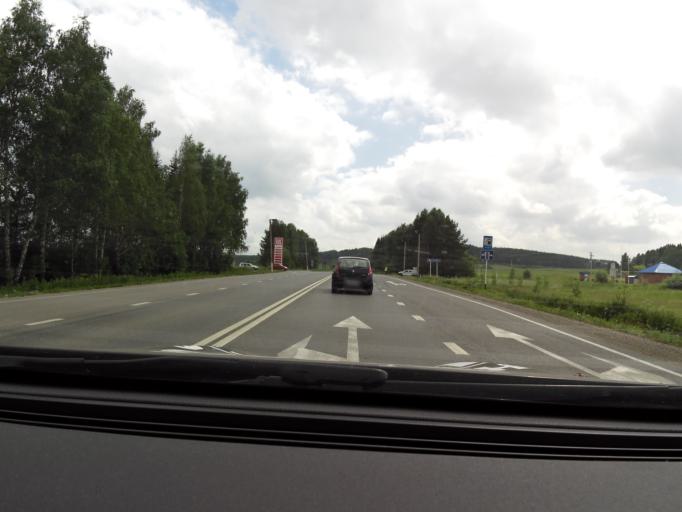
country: RU
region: Perm
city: Kungur
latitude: 57.4594
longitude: 56.7630
